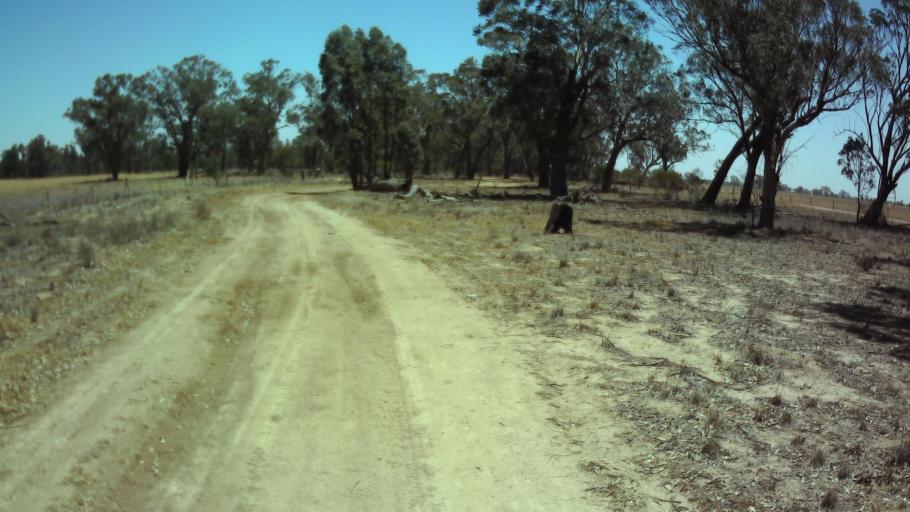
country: AU
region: New South Wales
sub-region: Weddin
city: Grenfell
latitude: -34.0589
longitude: 147.8148
